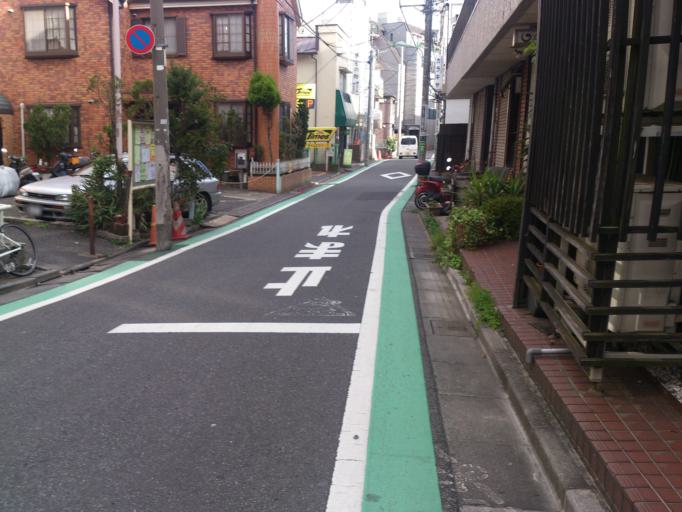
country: JP
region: Tokyo
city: Tokyo
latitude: 35.6713
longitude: 139.6833
